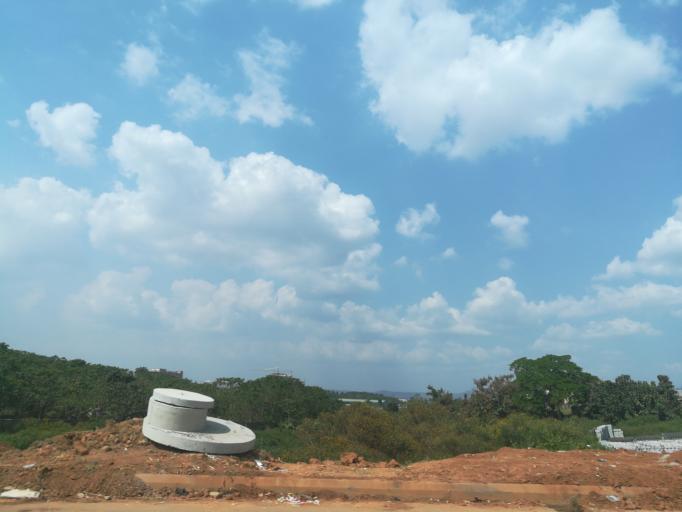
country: NG
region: Abuja Federal Capital Territory
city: Abuja
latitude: 9.0543
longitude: 7.4354
